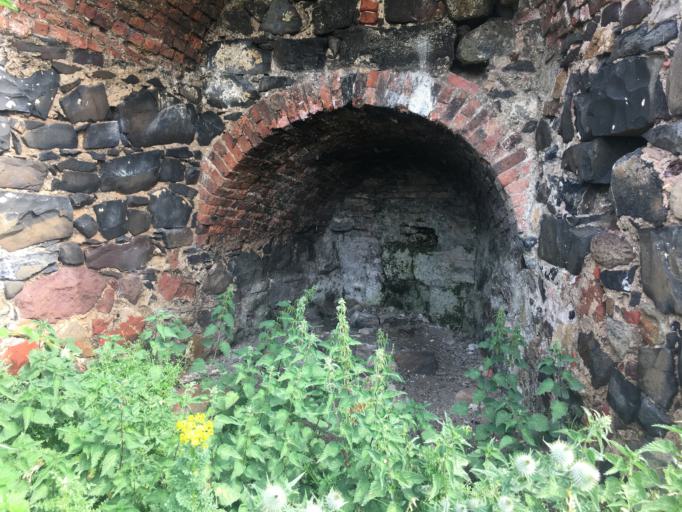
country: GB
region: England
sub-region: Northumberland
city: Bamburgh
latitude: 55.6114
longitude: -1.7575
